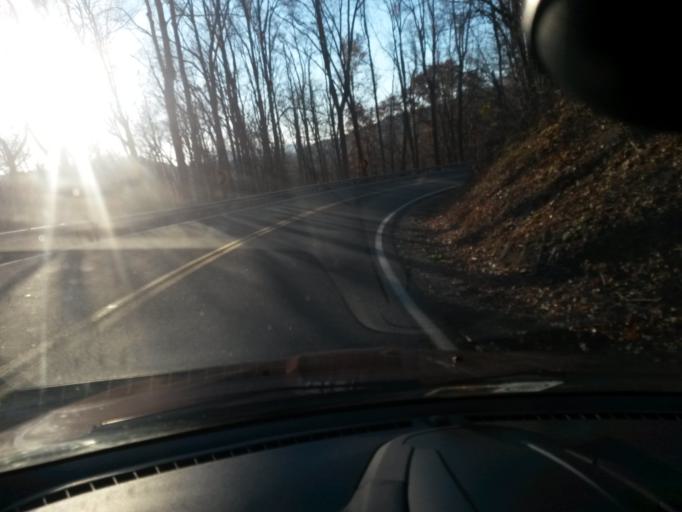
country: US
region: Virginia
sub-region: City of Buena Vista
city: Buena Vista
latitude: 37.7015
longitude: -79.2438
